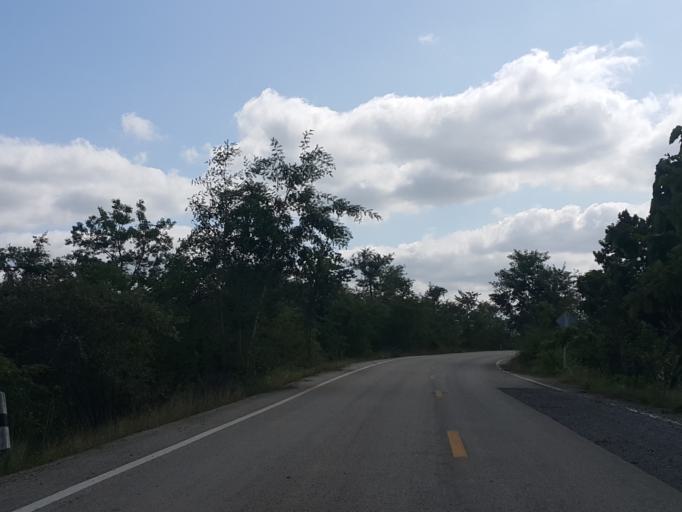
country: TH
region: Lamphun
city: Mae Tha
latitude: 18.5350
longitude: 99.0863
